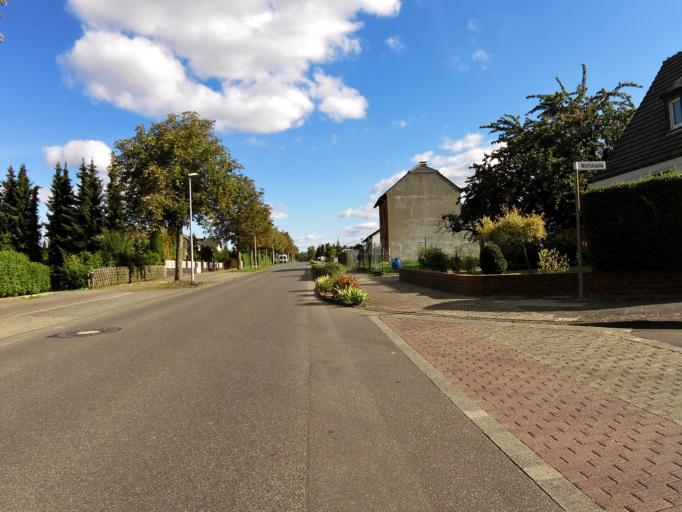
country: DE
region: North Rhine-Westphalia
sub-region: Regierungsbezirk Koln
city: Euskirchen
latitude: 50.6223
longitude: 6.8573
